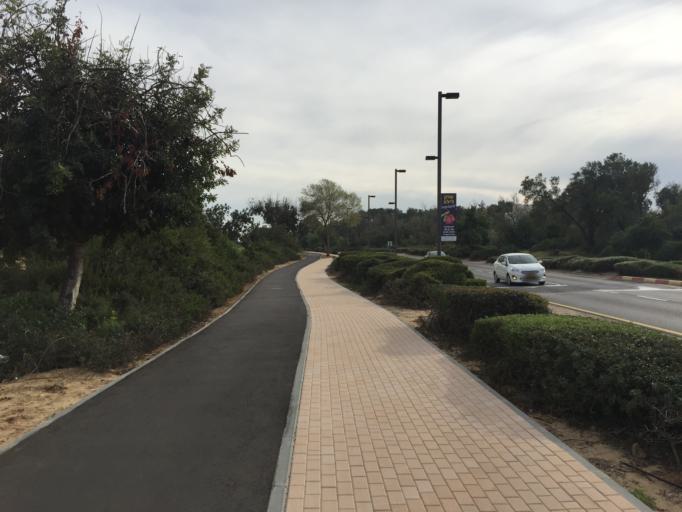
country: IL
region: Haifa
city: Qesarya
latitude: 32.5093
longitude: 34.9044
